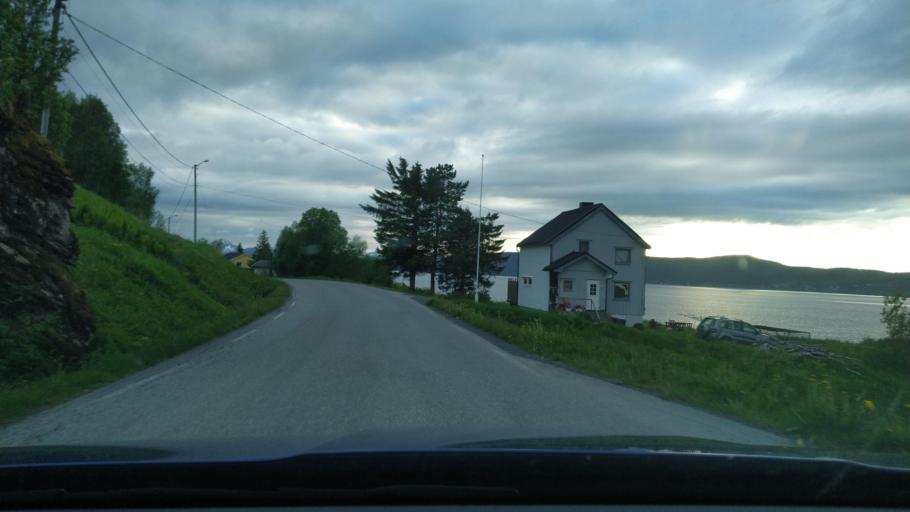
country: NO
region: Troms
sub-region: Tranoy
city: Vangsvika
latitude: 69.1276
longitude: 17.8479
